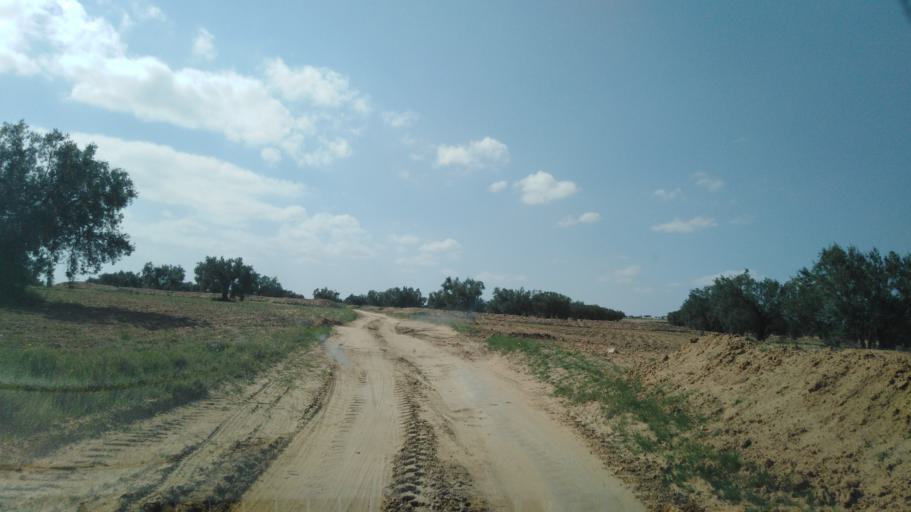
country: TN
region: Safaqis
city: Bi'r `Ali Bin Khalifah
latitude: 34.7930
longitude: 10.3984
